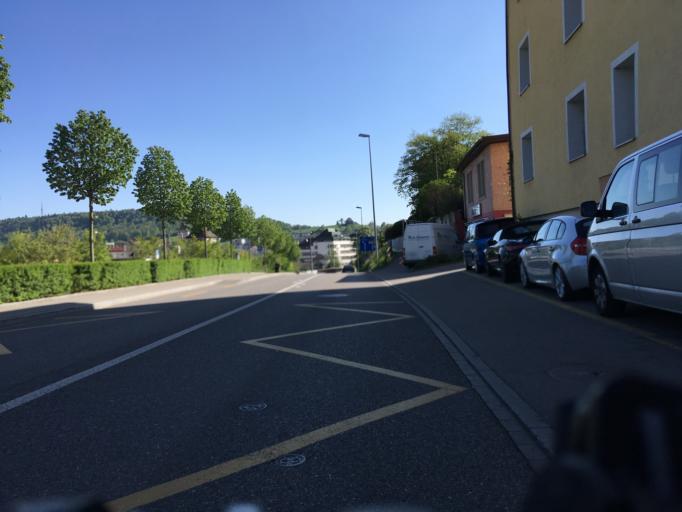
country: CH
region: Schaffhausen
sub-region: Bezirk Schaffhausen
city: Schaffhausen
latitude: 47.7023
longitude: 8.6349
